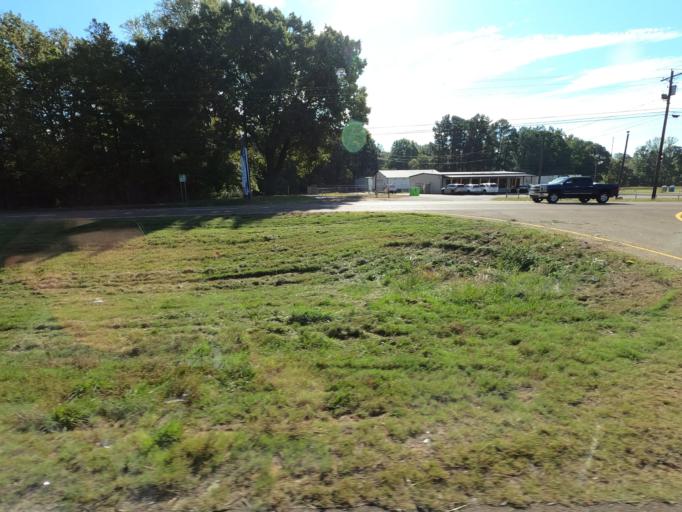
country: US
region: Tennessee
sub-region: Tipton County
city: Munford
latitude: 35.3952
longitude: -89.8513
